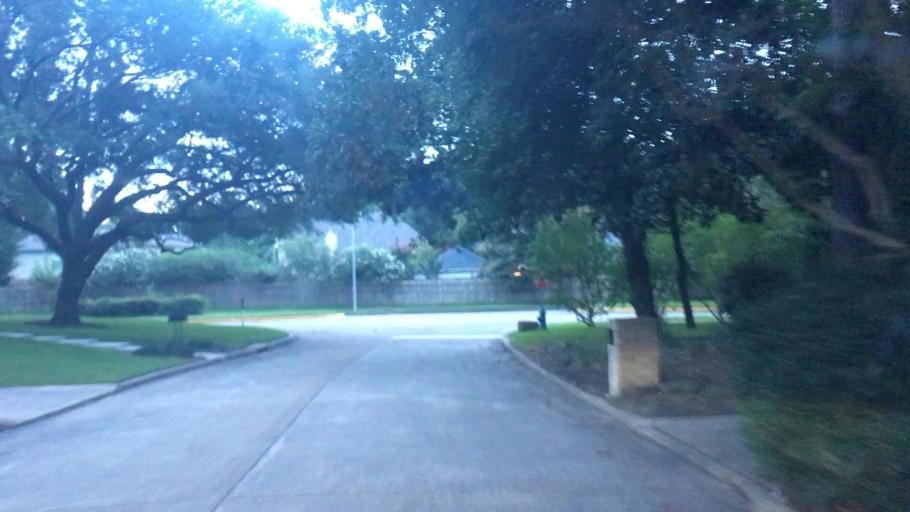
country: US
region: Texas
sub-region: Harris County
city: Atascocita
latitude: 30.0077
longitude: -95.1677
